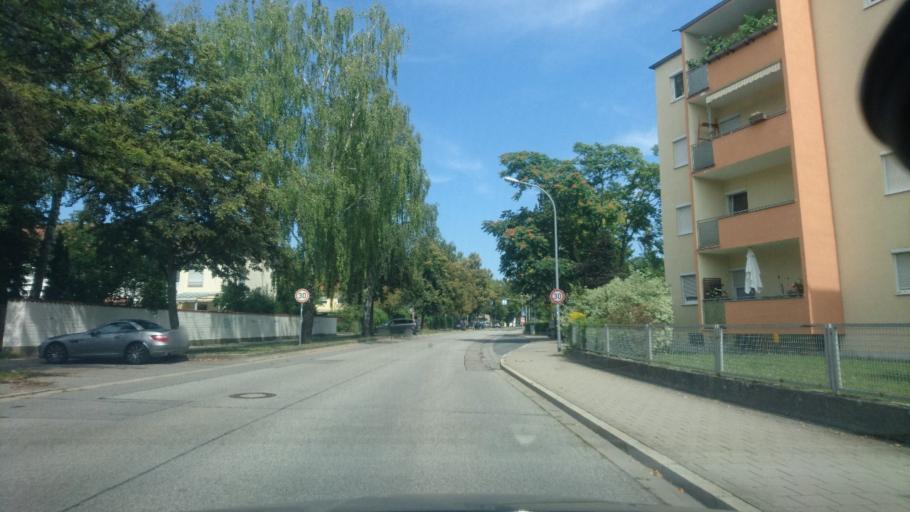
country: DE
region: Bavaria
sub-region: Upper Palatinate
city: Sinzing
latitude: 49.0132
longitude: 12.0465
